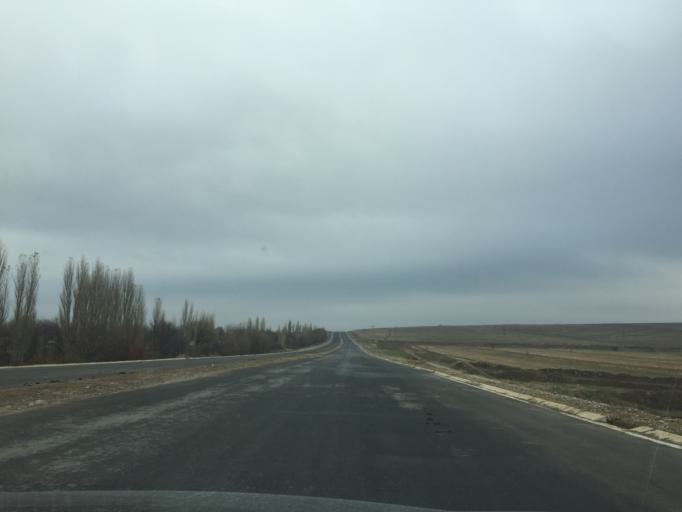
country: KZ
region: Ongtustik Qazaqstan
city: Kokterek
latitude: 42.5493
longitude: 70.1648
